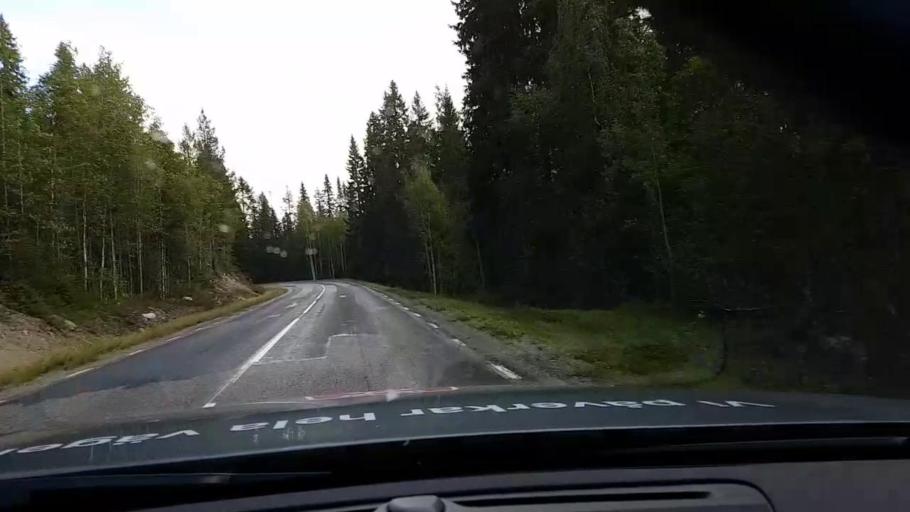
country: SE
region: Vaesterbotten
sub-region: Asele Kommun
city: Asele
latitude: 63.8360
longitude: 17.4380
